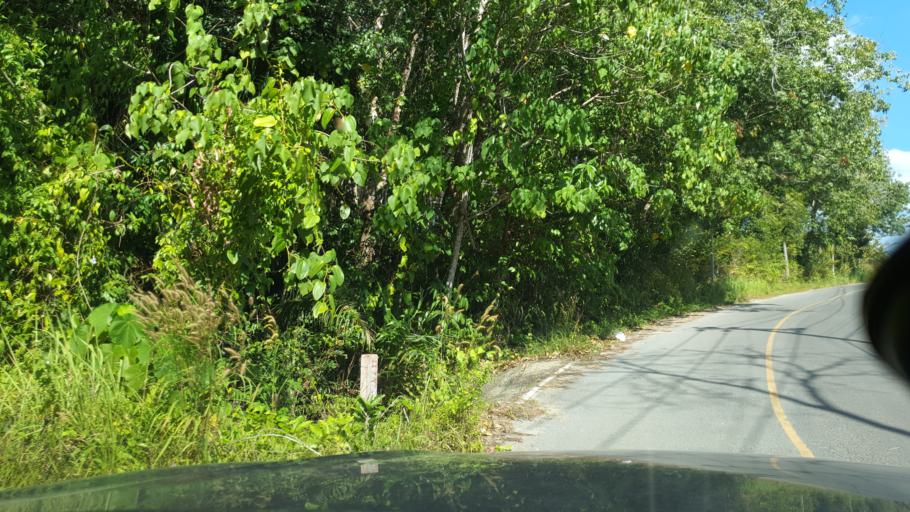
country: TH
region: Phangnga
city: Ban Ao Nang
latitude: 8.0284
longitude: 98.8558
